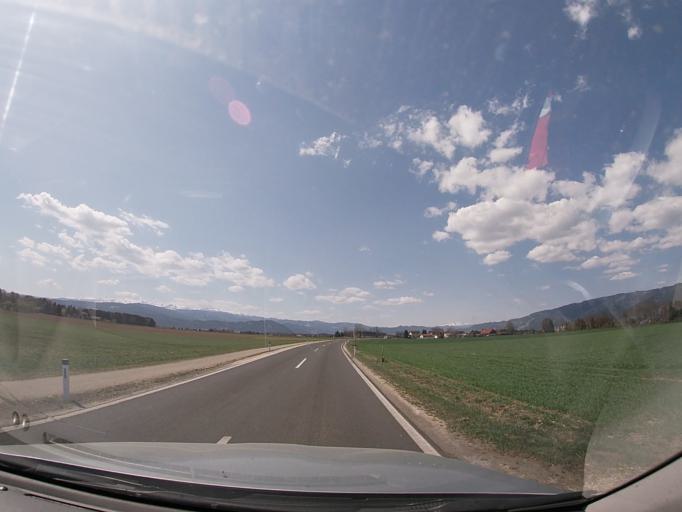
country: AT
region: Styria
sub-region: Politischer Bezirk Murtal
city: Grosslobming
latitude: 47.1812
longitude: 14.7832
